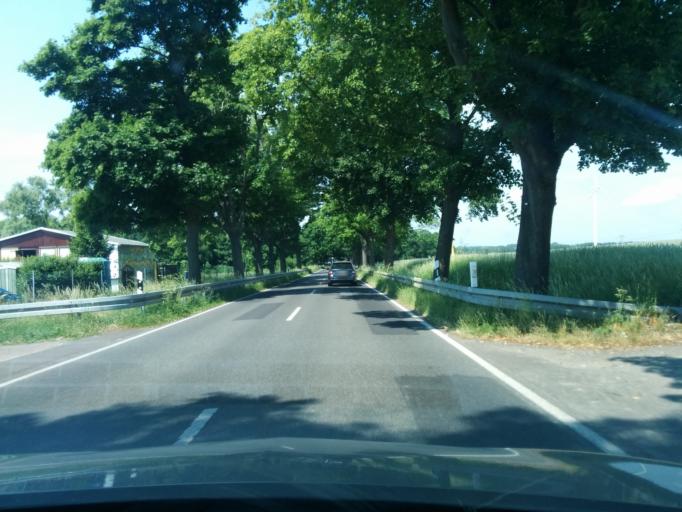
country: DE
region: Brandenburg
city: Ahrensfelde
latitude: 52.6118
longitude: 13.5950
